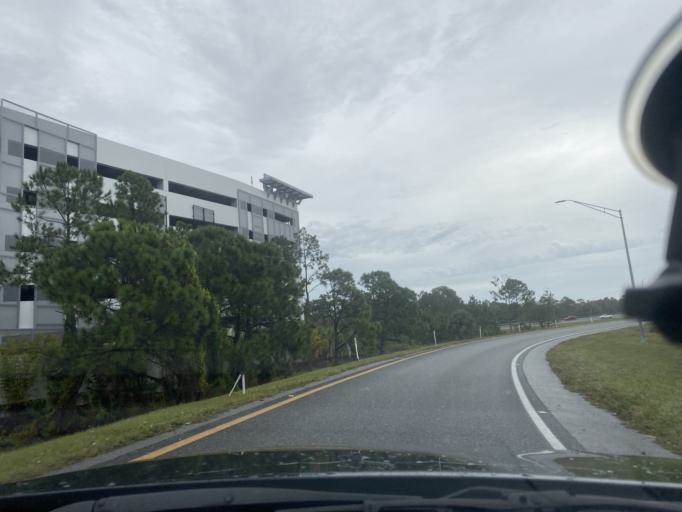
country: US
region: Florida
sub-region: Orange County
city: Alafaya
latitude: 28.5677
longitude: -81.1935
